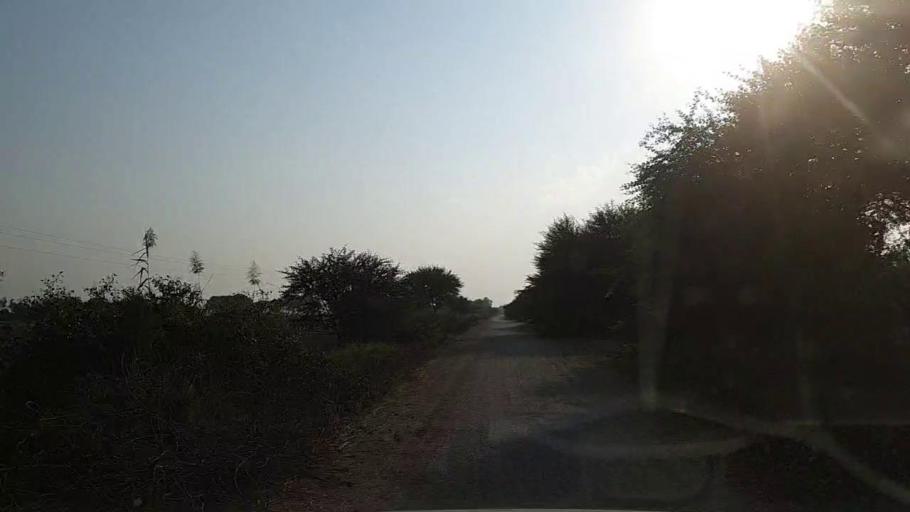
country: PK
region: Sindh
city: Mirpur Batoro
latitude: 24.7797
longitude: 68.2424
